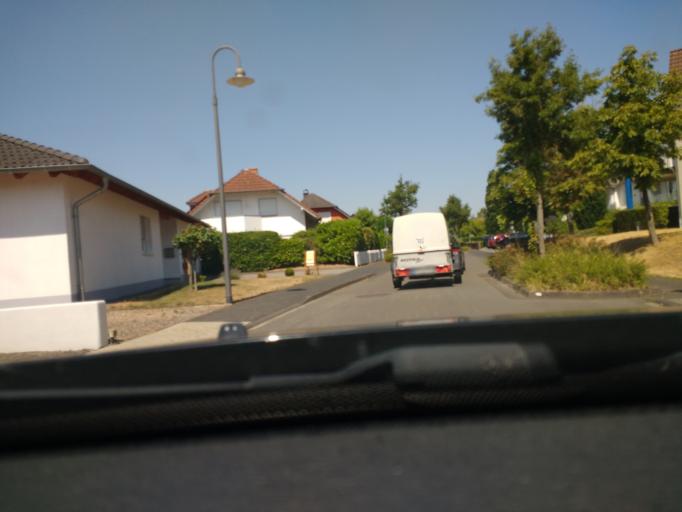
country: DE
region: Rheinland-Pfalz
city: Altrich
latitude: 49.9738
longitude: 6.9326
